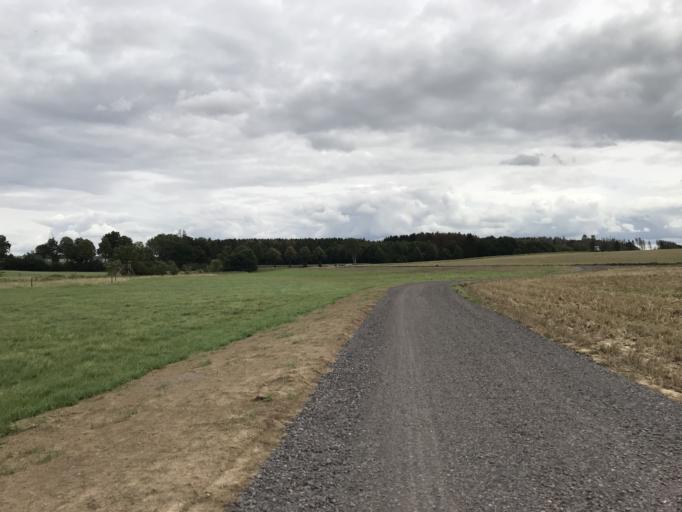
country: DE
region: Hesse
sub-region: Regierungsbezirk Giessen
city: Grunberg
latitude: 50.6309
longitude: 8.9546
